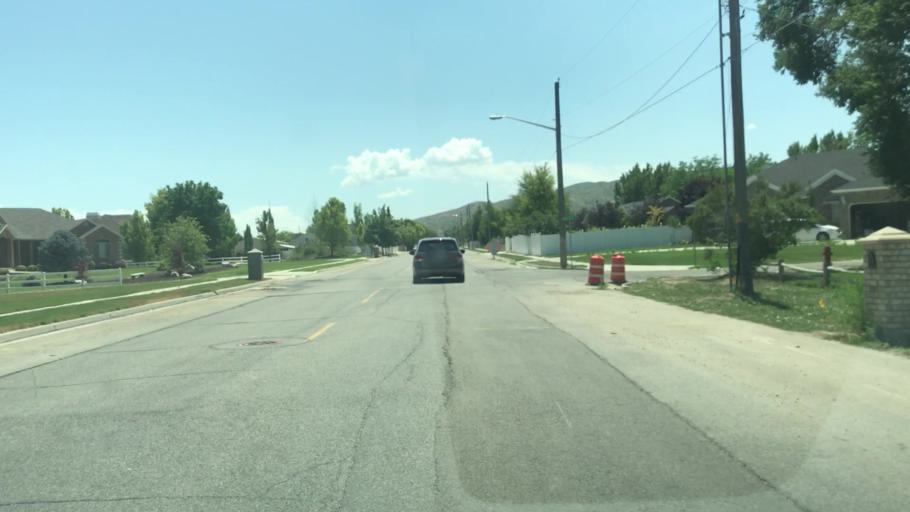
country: US
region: Utah
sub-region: Salt Lake County
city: Bluffdale
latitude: 40.4849
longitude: -111.9484
